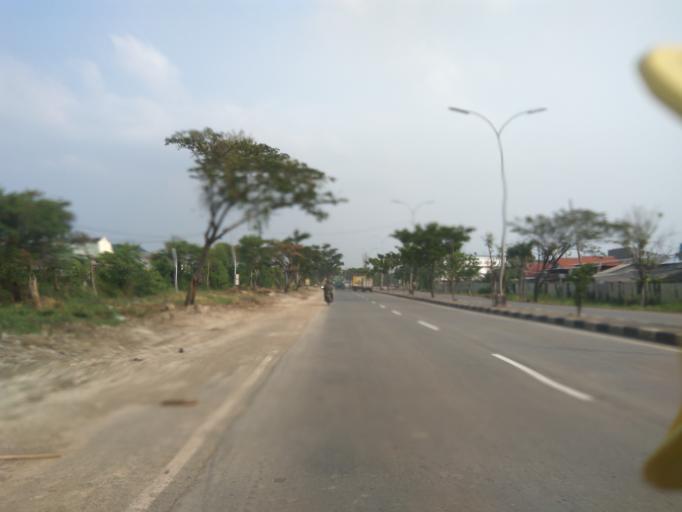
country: ID
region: Central Java
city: Semarang
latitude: -6.9646
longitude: 110.3940
